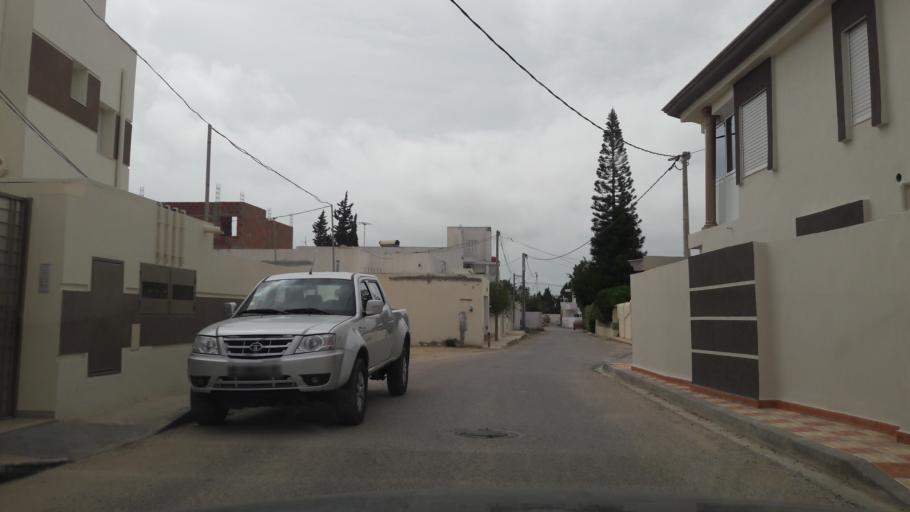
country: TN
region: Safaqis
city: Sfax
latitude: 34.7724
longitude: 10.7561
